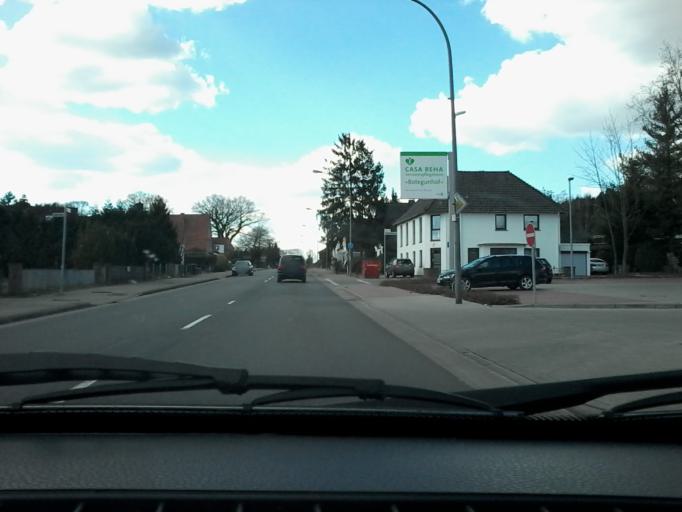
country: DE
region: Lower Saxony
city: Ahsen-Oetzen
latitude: 52.9997
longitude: 9.0682
